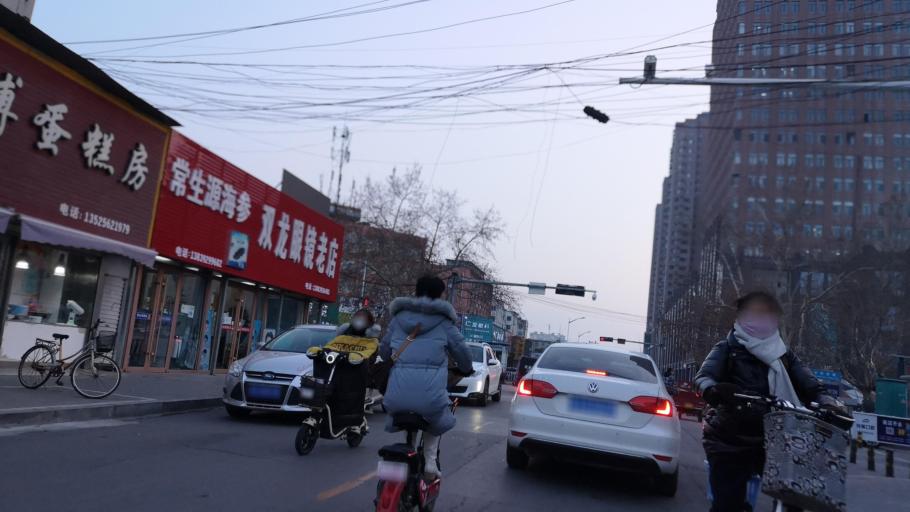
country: CN
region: Henan Sheng
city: Zhongyuanlu
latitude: 35.7756
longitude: 115.0812
